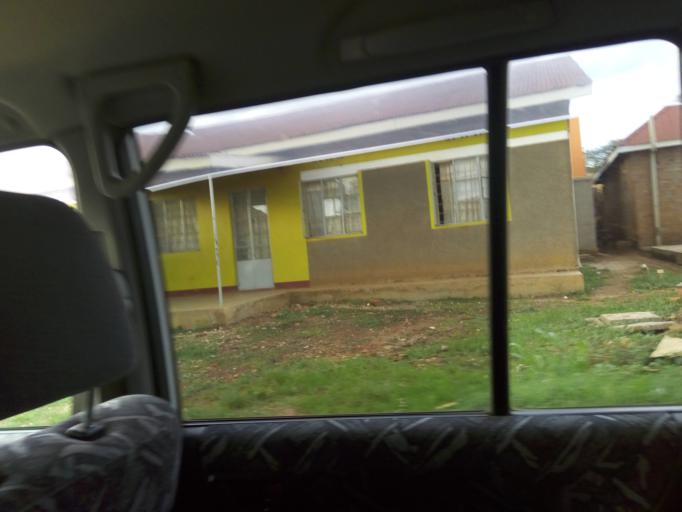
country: UG
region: Western Region
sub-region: Masindi District
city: Masindi
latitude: 1.6823
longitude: 31.7171
